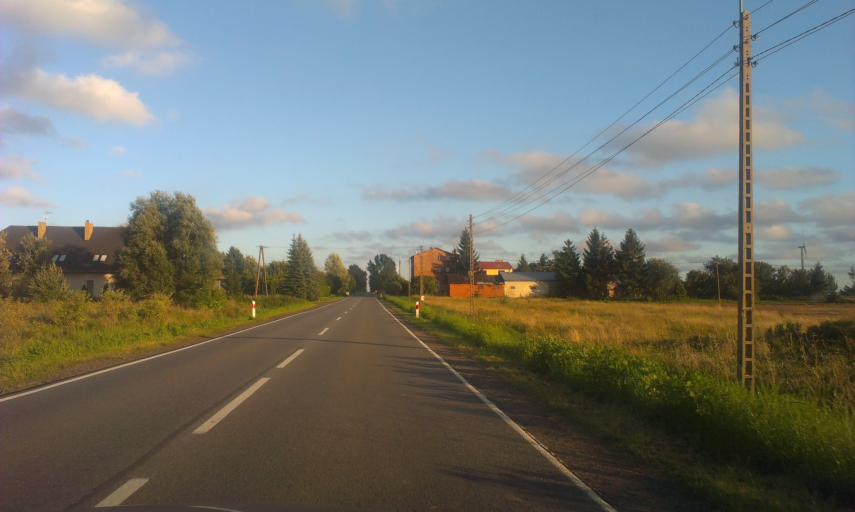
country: PL
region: West Pomeranian Voivodeship
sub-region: Powiat slawienski
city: Slawno
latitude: 54.3439
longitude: 16.5409
